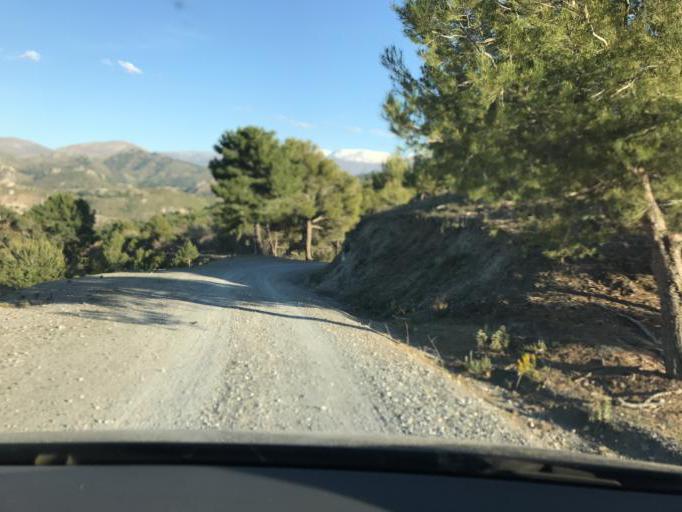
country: ES
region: Andalusia
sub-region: Provincia de Granada
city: Beas de Granada
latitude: 37.2360
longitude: -3.4237
